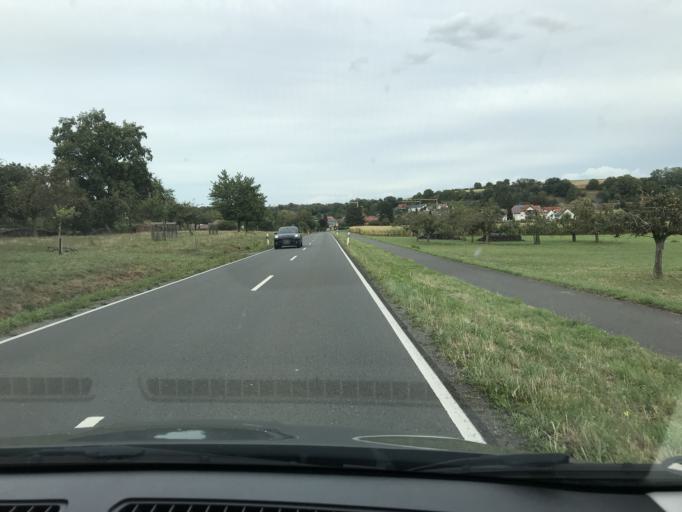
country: DE
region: Hesse
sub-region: Regierungsbezirk Darmstadt
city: Schaafheim
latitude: 49.9111
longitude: 8.9657
